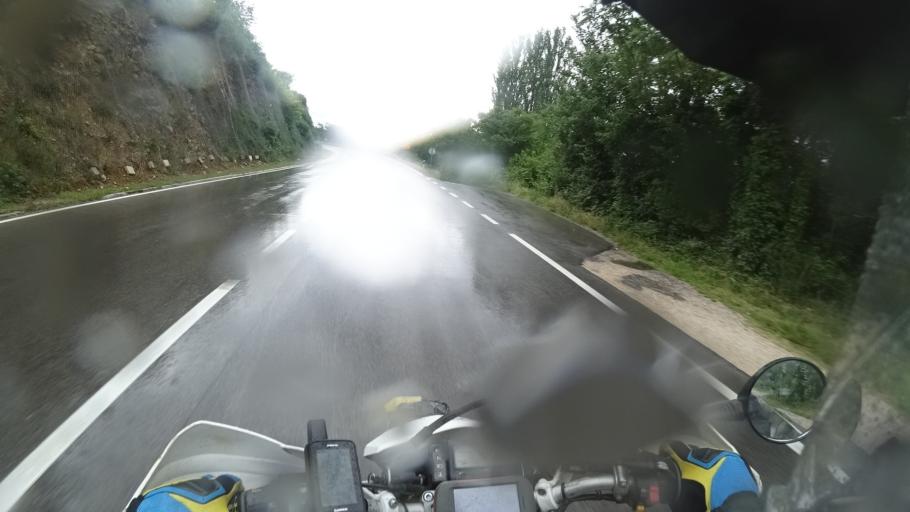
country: HR
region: Sibensko-Kniniska
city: Knin
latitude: 44.0419
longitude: 16.1870
